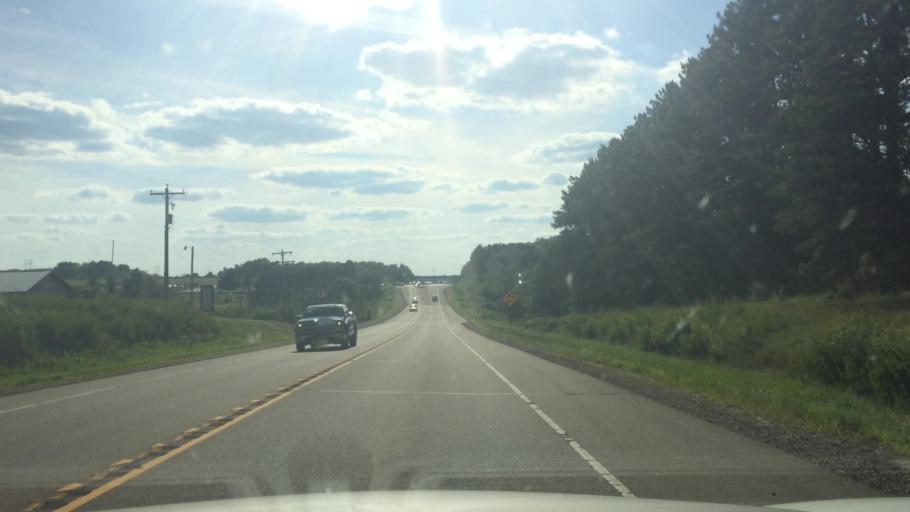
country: US
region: Wisconsin
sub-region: Lincoln County
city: Merrill
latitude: 45.1779
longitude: -89.6355
